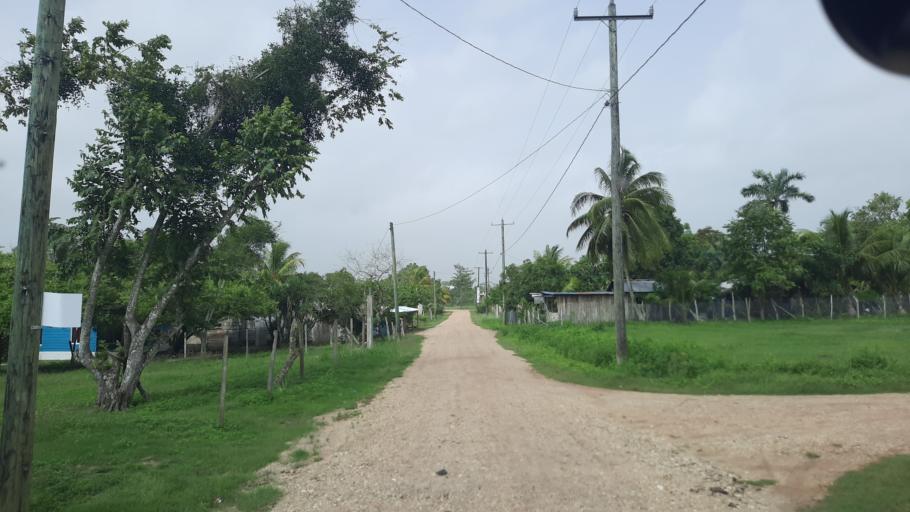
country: BZ
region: Cayo
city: Valley of Peace
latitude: 17.2509
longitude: -88.9409
